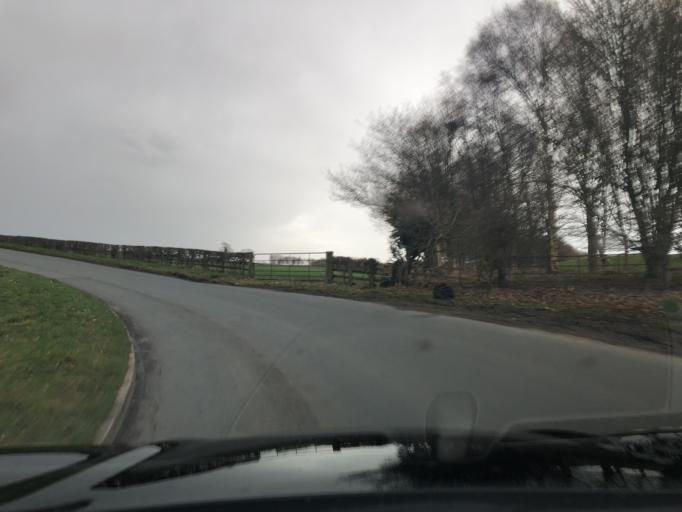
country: GB
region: England
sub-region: North Yorkshire
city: Northallerton
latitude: 54.3439
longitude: -1.4644
